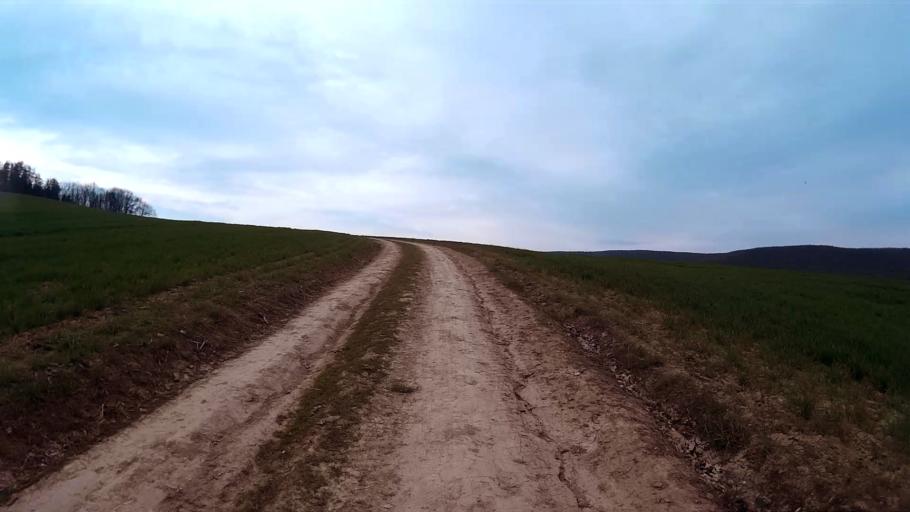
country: CZ
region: South Moravian
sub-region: Mesto Brno
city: Mokra Hora
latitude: 49.2436
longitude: 16.5450
